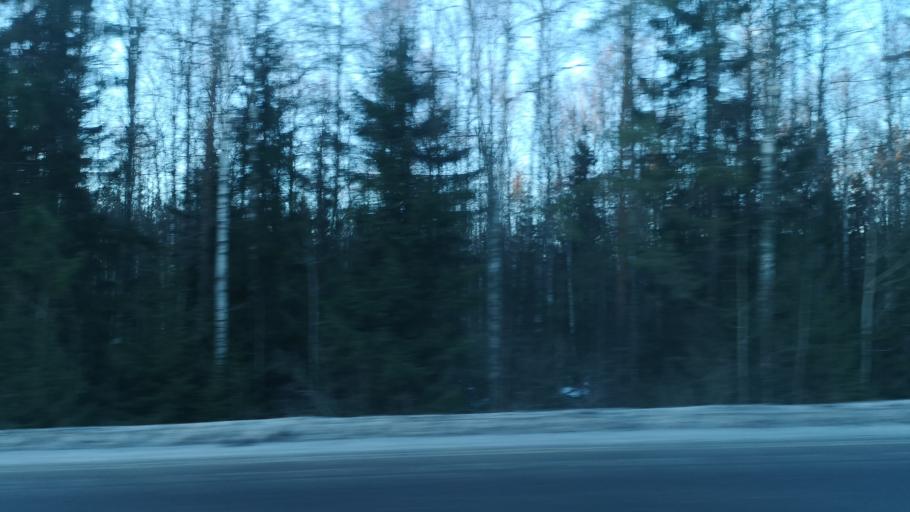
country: FI
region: Southern Savonia
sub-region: Pieksaemaeki
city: Juva
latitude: 61.9263
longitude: 28.0445
